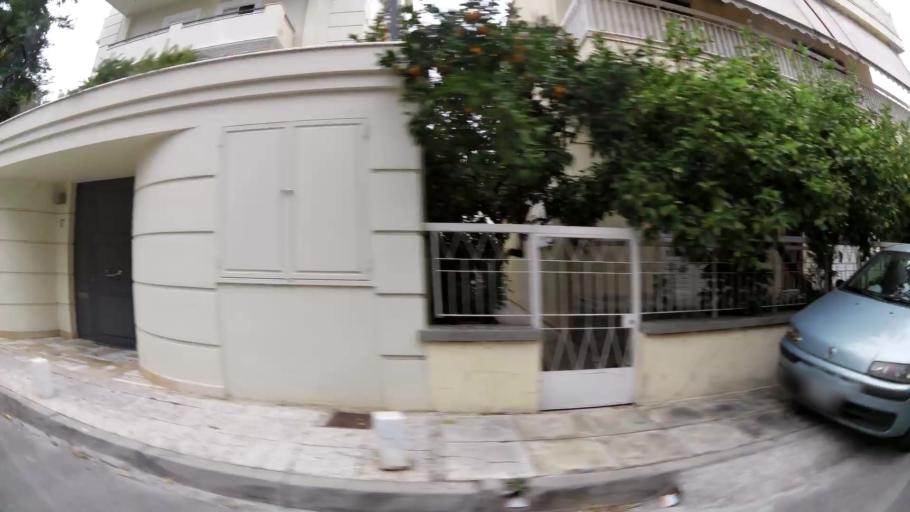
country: GR
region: Attica
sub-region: Nomarchia Athinas
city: Alimos
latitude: 37.9145
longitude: 23.7296
